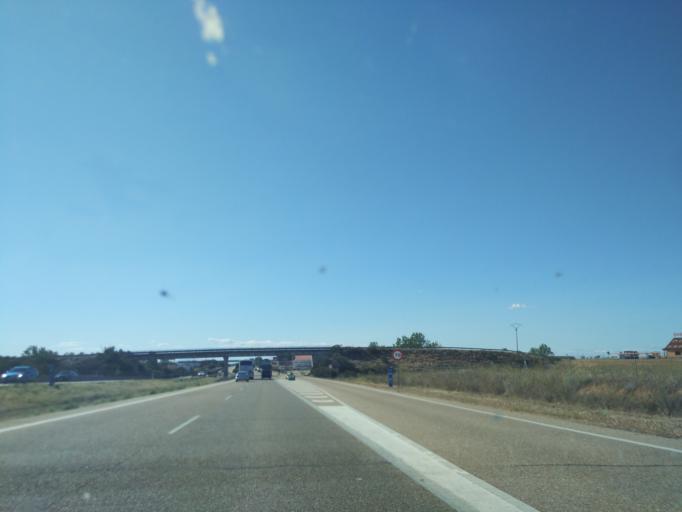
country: ES
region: Castille and Leon
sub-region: Provincia de Zamora
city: San Esteban del Molar
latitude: 41.9365
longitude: -5.5440
